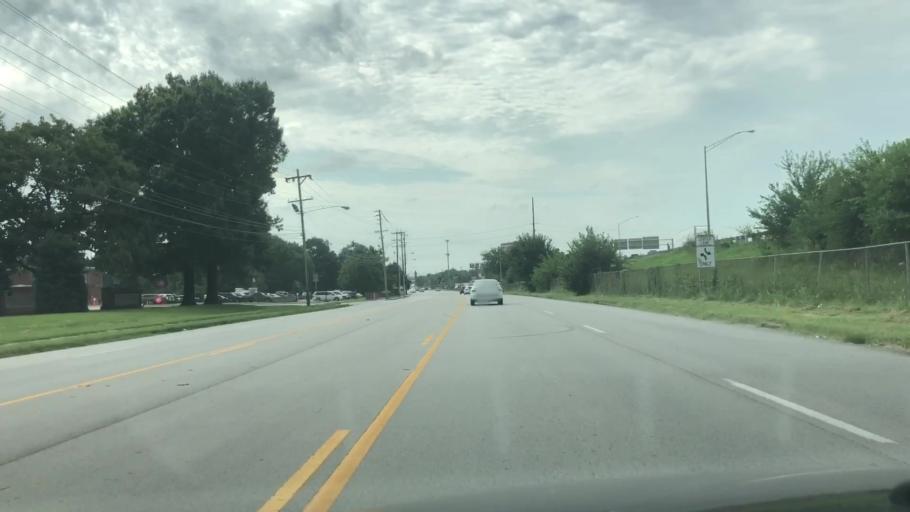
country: US
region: Kentucky
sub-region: Jefferson County
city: Audubon Park
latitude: 38.1844
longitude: -85.7228
